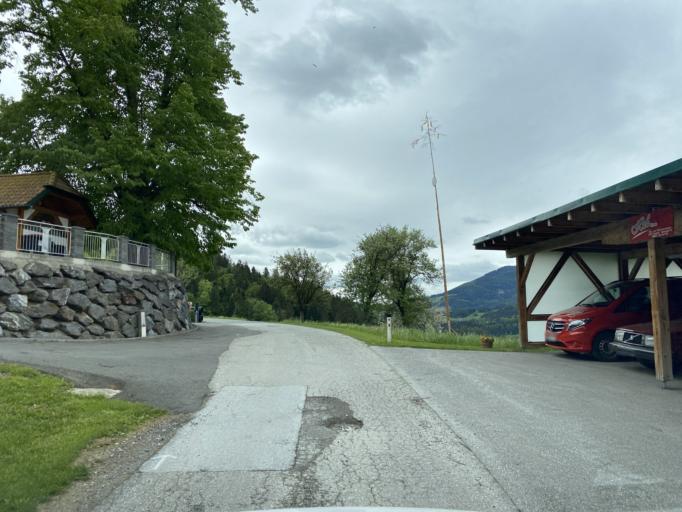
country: AT
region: Styria
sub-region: Politischer Bezirk Weiz
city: Koglhof
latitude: 47.3281
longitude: 15.7000
